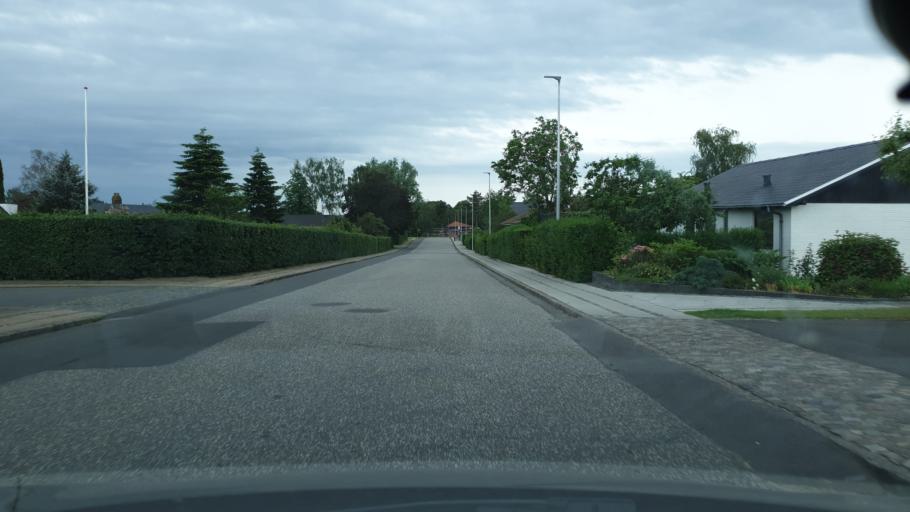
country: DK
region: South Denmark
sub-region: Kolding Kommune
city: Kolding
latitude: 55.5047
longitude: 9.4960
